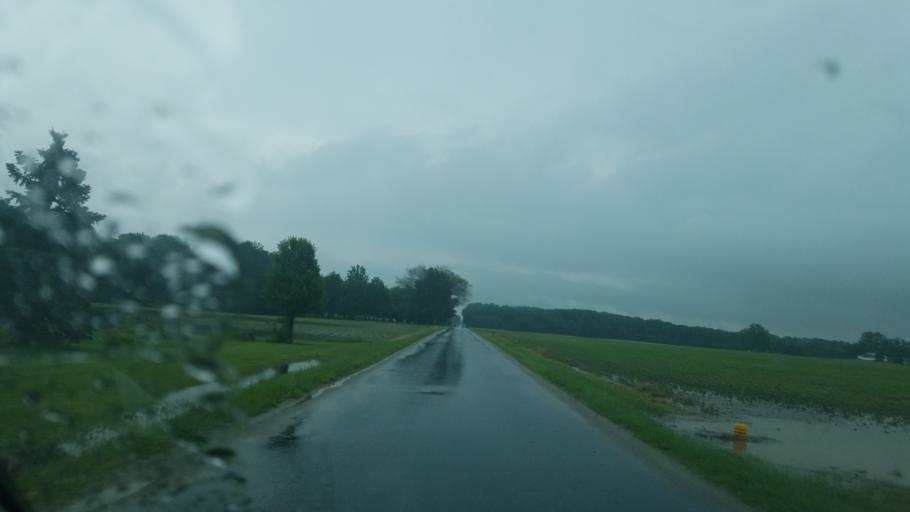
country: US
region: Ohio
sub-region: Huron County
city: Plymouth
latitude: 40.9449
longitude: -82.6928
